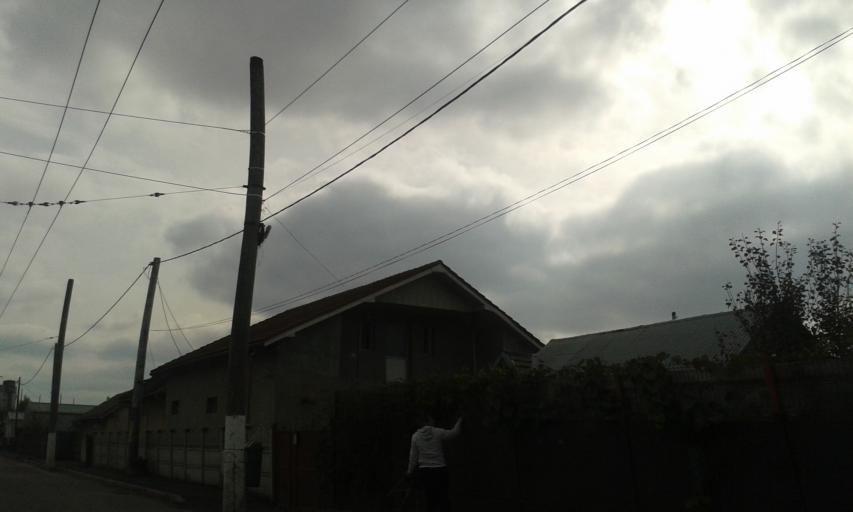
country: RO
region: Gorj
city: Targu Jiu
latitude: 45.0756
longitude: 23.3004
